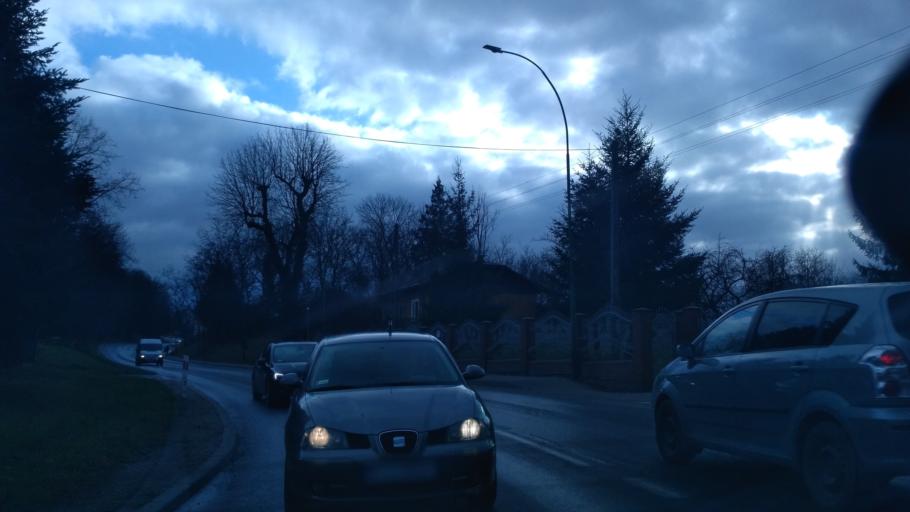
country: PL
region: Subcarpathian Voivodeship
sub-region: Powiat lancucki
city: Lancut
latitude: 50.0797
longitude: 22.2328
